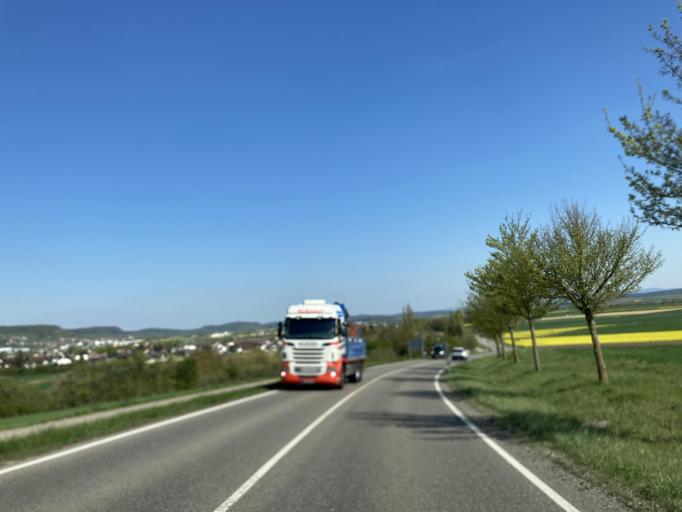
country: DE
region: Baden-Wuerttemberg
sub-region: Regierungsbezirk Stuttgart
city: Herrenberg
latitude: 48.5747
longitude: 8.8640
